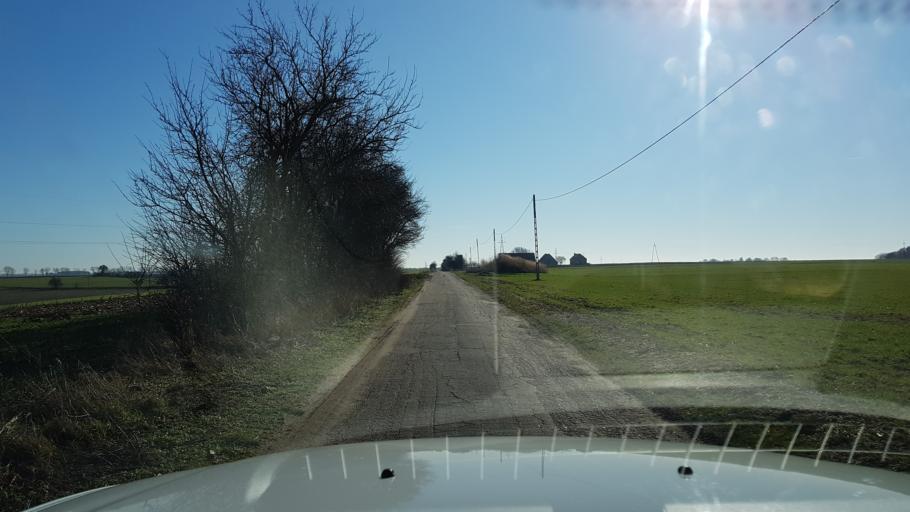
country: PL
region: West Pomeranian Voivodeship
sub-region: Powiat pyrzycki
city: Przelewice
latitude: 53.0493
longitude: 15.0595
